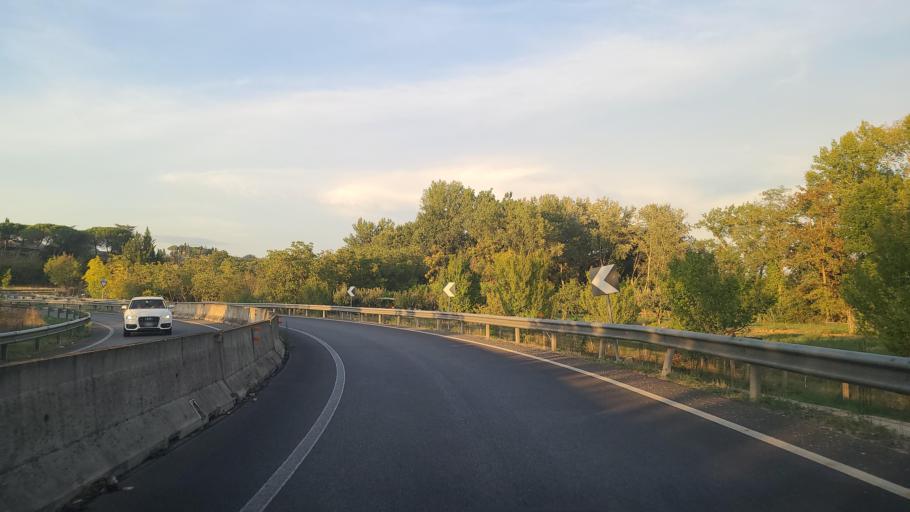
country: IT
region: Tuscany
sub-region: Provincia di Siena
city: Poggibonsi
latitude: 43.4850
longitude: 11.1555
